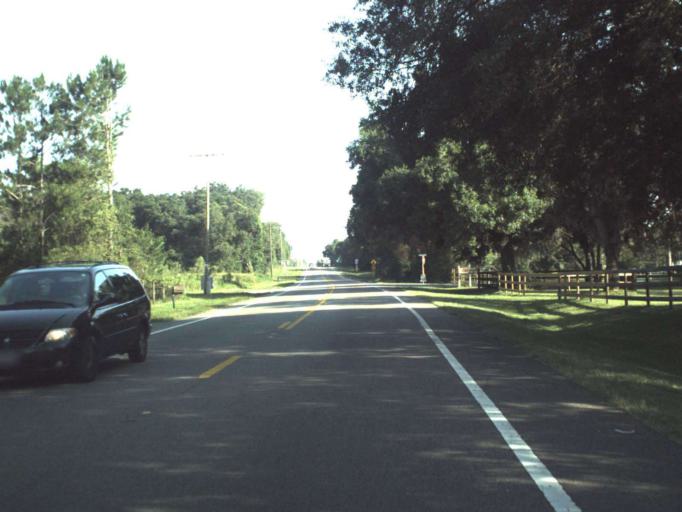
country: US
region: Florida
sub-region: Lake County
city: Groveland
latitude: 28.4124
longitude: -81.8309
